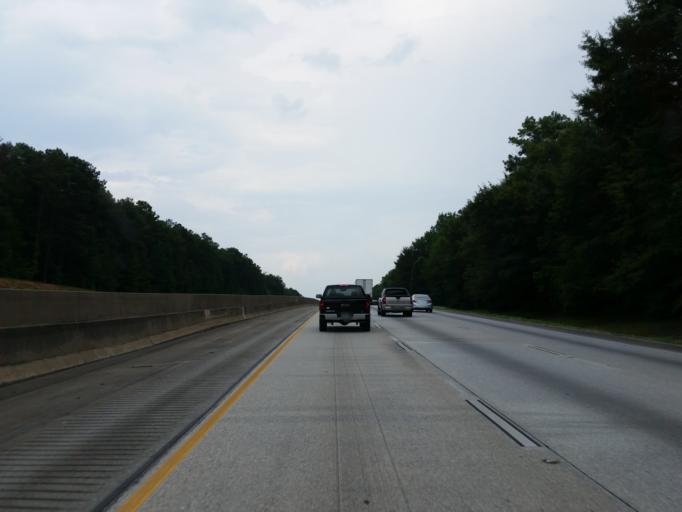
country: US
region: Georgia
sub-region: Monroe County
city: Forsyth
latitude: 33.0169
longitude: -83.8888
